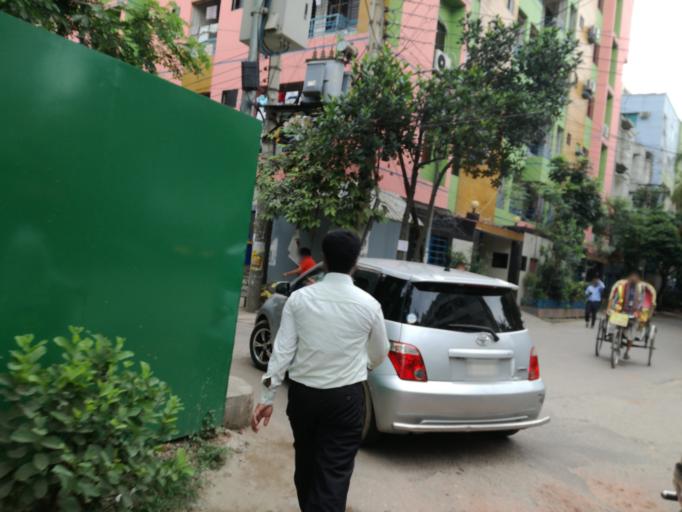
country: BD
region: Dhaka
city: Paltan
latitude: 23.7727
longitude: 90.4135
